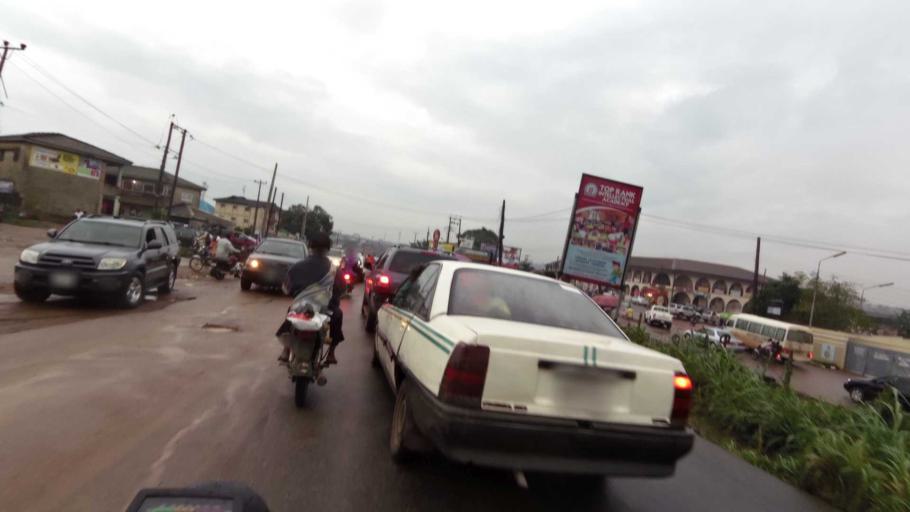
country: NG
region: Oyo
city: Ibadan
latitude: 7.4248
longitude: 3.9376
